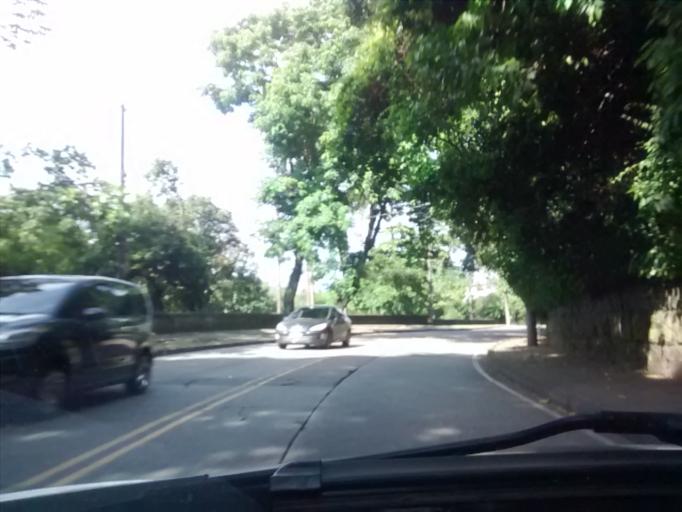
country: BR
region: Rio de Janeiro
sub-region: Rio De Janeiro
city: Rio de Janeiro
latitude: -22.9549
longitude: -43.2648
